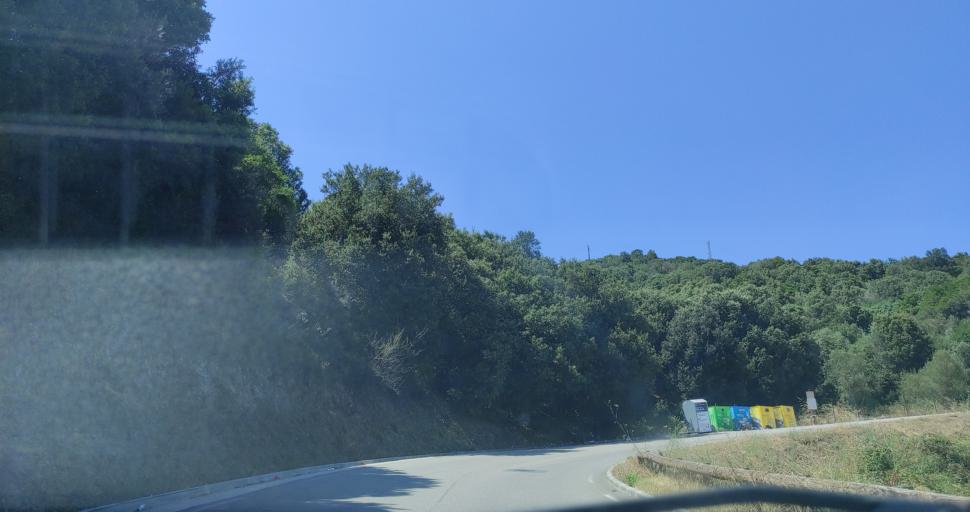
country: FR
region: Corsica
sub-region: Departement de la Corse-du-Sud
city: Alata
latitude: 41.9581
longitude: 8.7264
